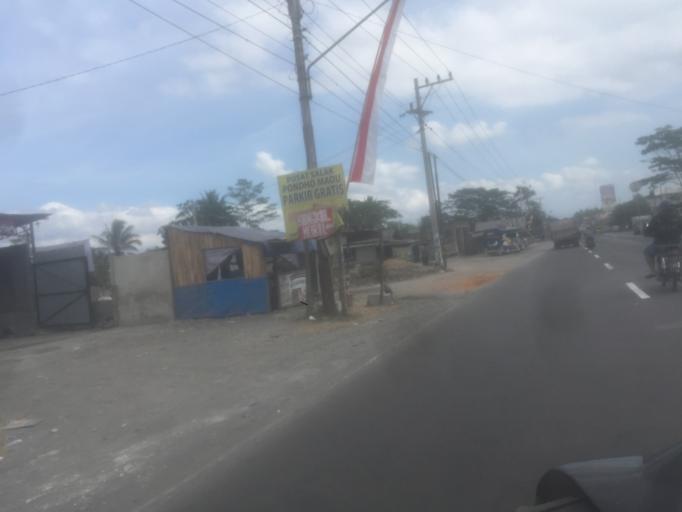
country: ID
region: Central Java
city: Muntilan
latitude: -7.6049
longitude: 110.3007
